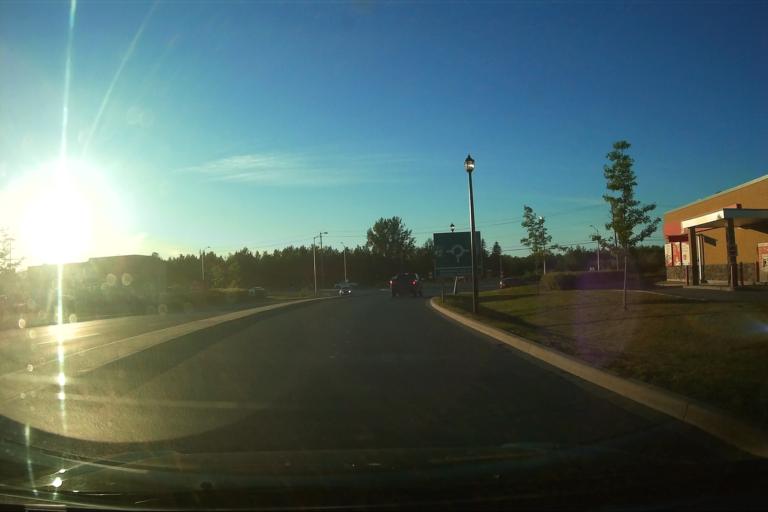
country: CA
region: Ontario
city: Prescott
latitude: 45.0300
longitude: -75.6329
